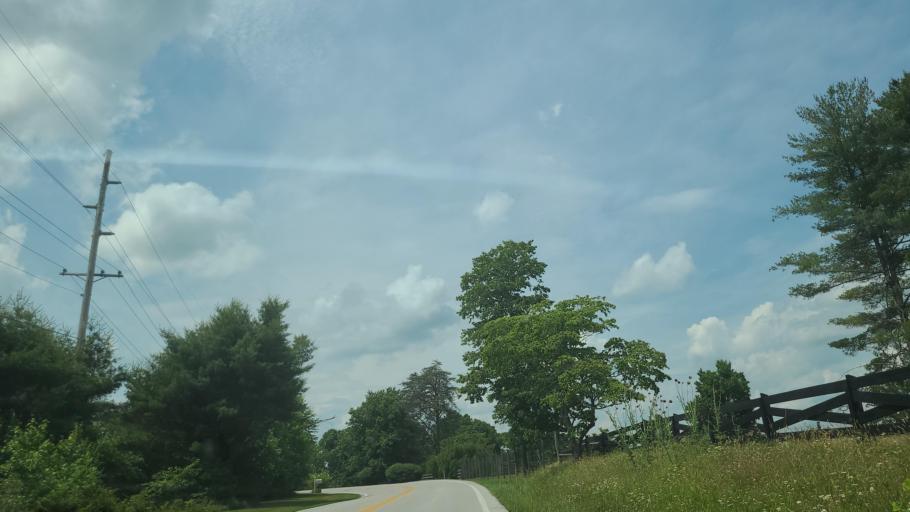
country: US
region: Tennessee
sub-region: Cumberland County
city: Crossville
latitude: 35.9042
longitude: -85.0024
